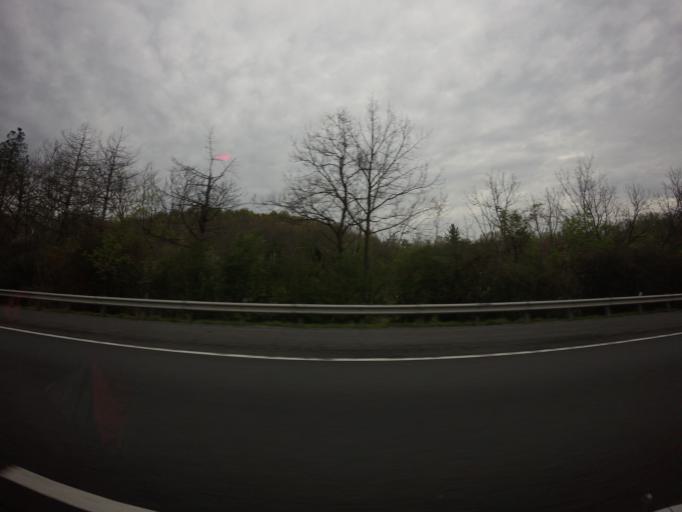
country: US
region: Maryland
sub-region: Carroll County
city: Mount Airy
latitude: 39.3655
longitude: -77.1860
